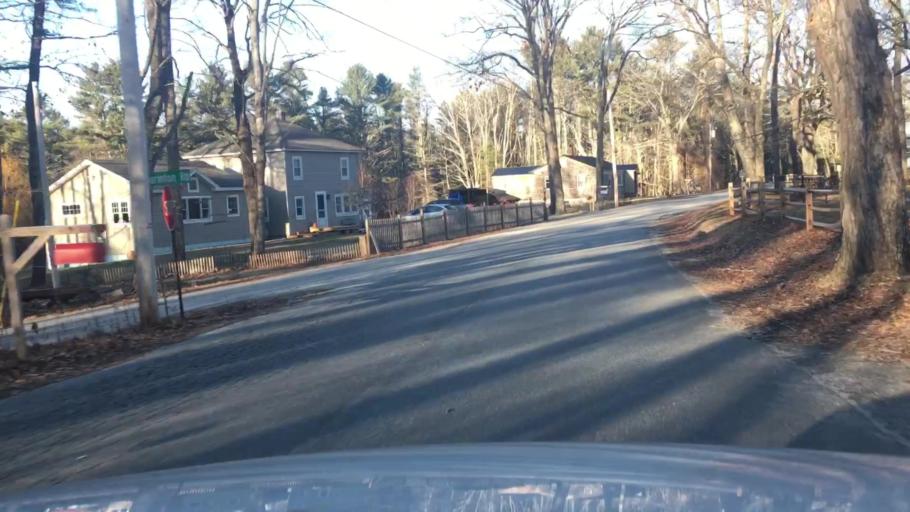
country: US
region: Maine
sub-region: Cumberland County
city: Brunswick
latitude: 43.8836
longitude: -69.9171
